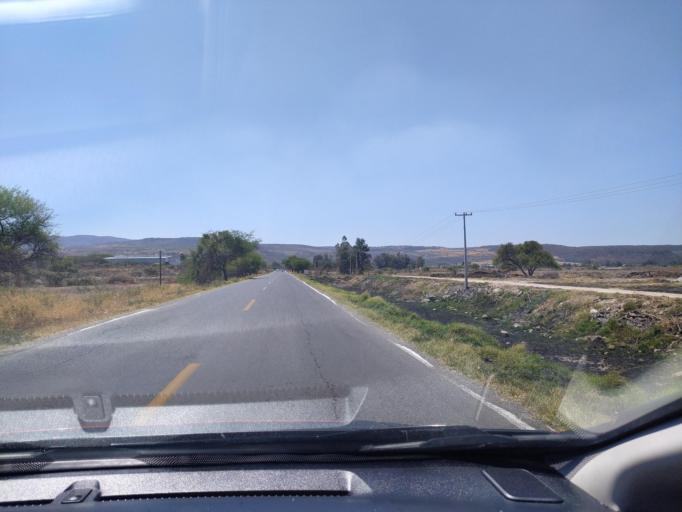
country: MX
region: Guanajuato
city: Ciudad Manuel Doblado
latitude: 20.7405
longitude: -101.9428
